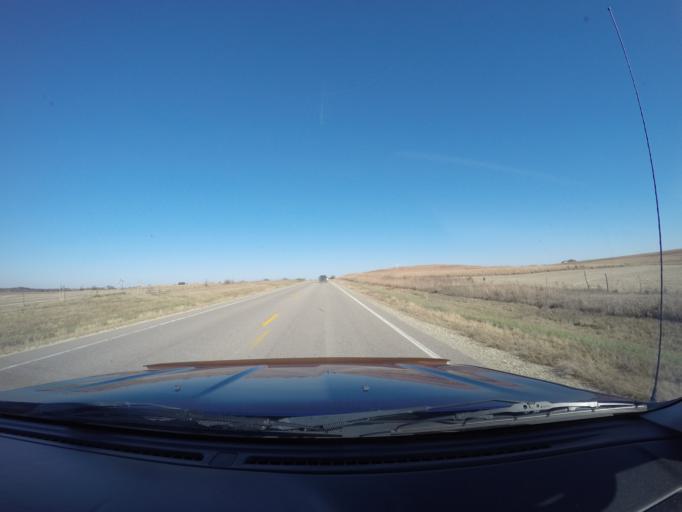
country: US
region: Kansas
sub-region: Riley County
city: Ogden
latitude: 39.3366
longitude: -96.7563
